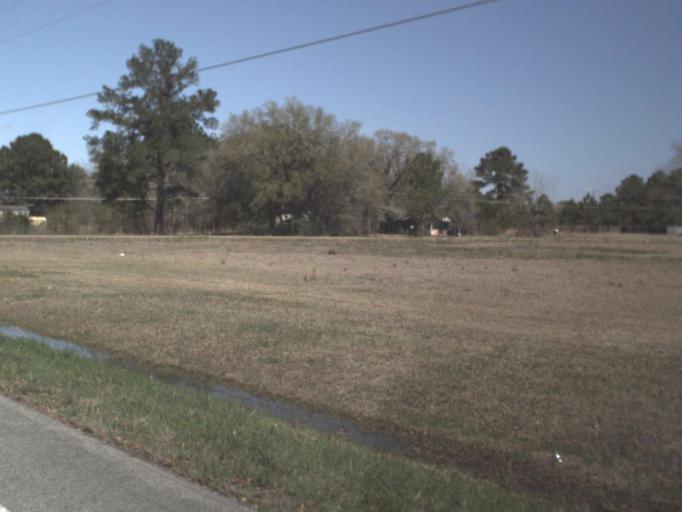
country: US
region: Florida
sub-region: Gadsden County
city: Gretna
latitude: 30.6925
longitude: -84.6227
